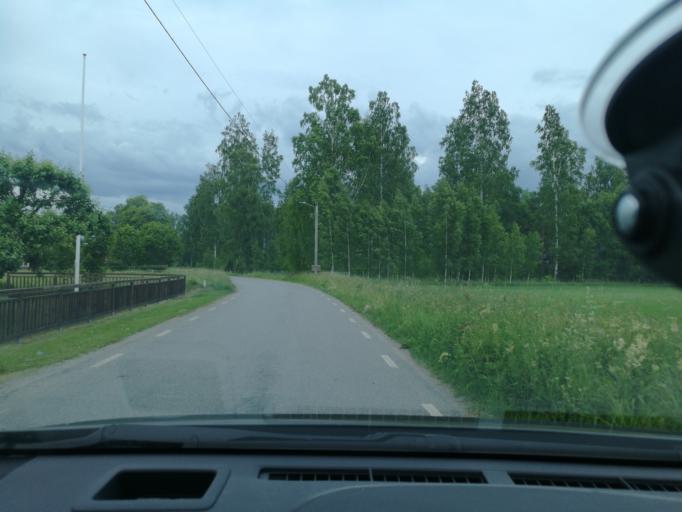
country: SE
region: Vaestmanland
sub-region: Vasteras
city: Skultuna
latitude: 59.8771
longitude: 16.3484
